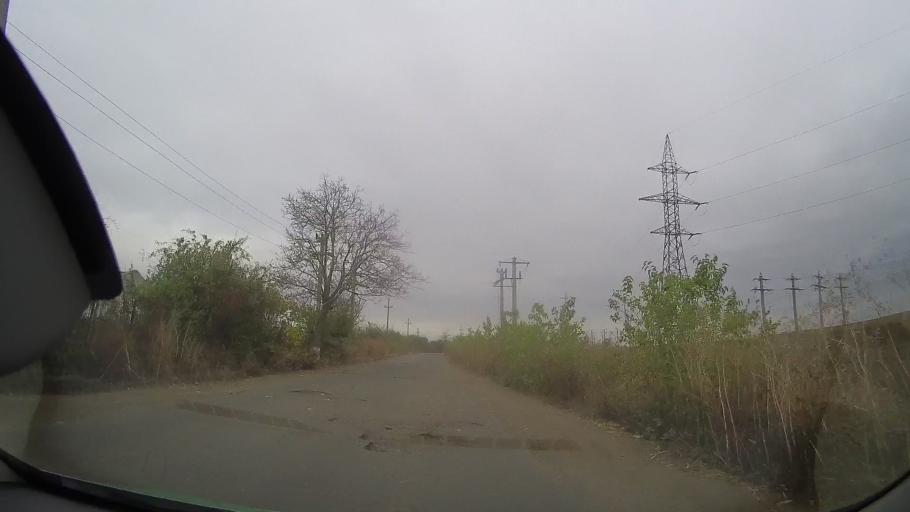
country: RO
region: Braila
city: Dudesti
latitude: 44.8948
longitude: 27.4346
